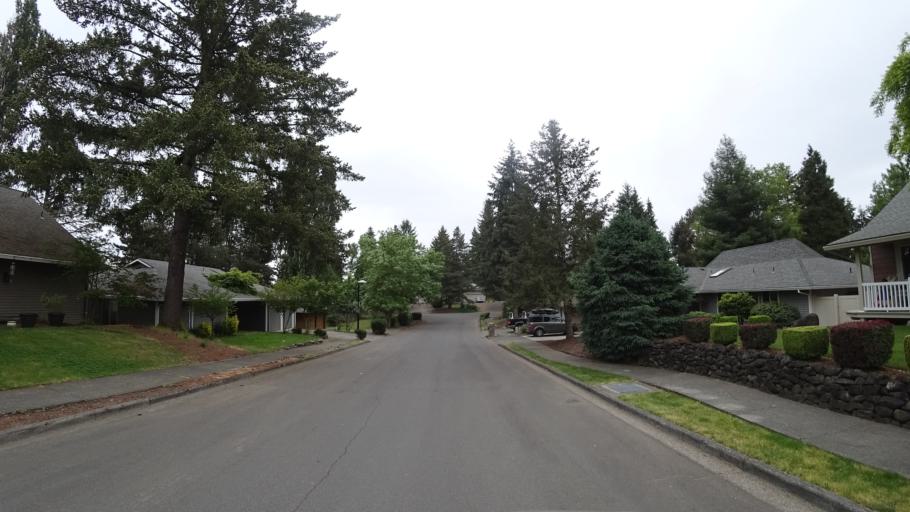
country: US
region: Oregon
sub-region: Washington County
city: Rockcreek
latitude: 45.5591
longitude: -122.8821
